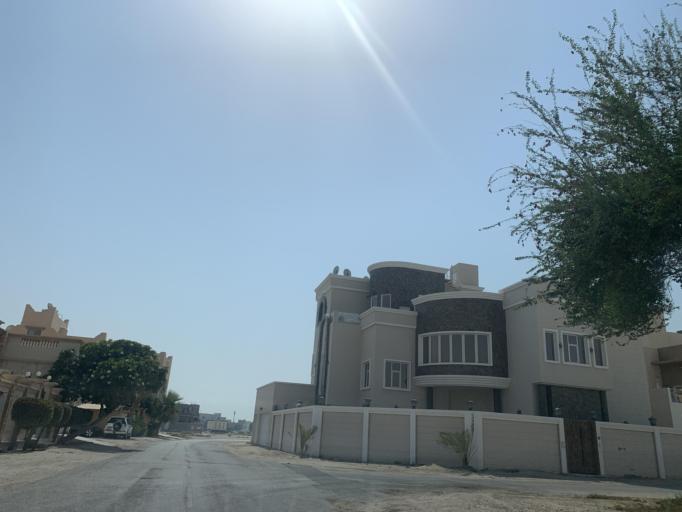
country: BH
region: Manama
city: Jidd Hafs
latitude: 26.2061
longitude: 50.5287
